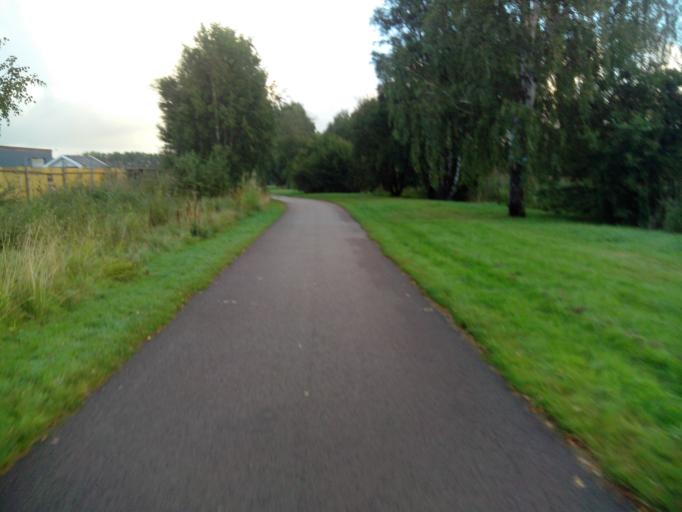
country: SE
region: Vaestra Goetaland
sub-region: Goteborg
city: Goeteborg
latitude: 57.7322
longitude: 11.9529
